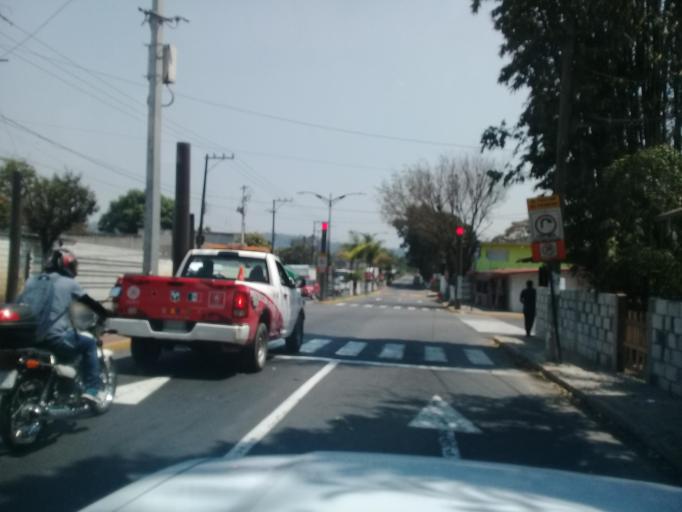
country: MX
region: Veracruz
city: Ixtac Zoquitlan
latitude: 18.8621
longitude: -97.0528
